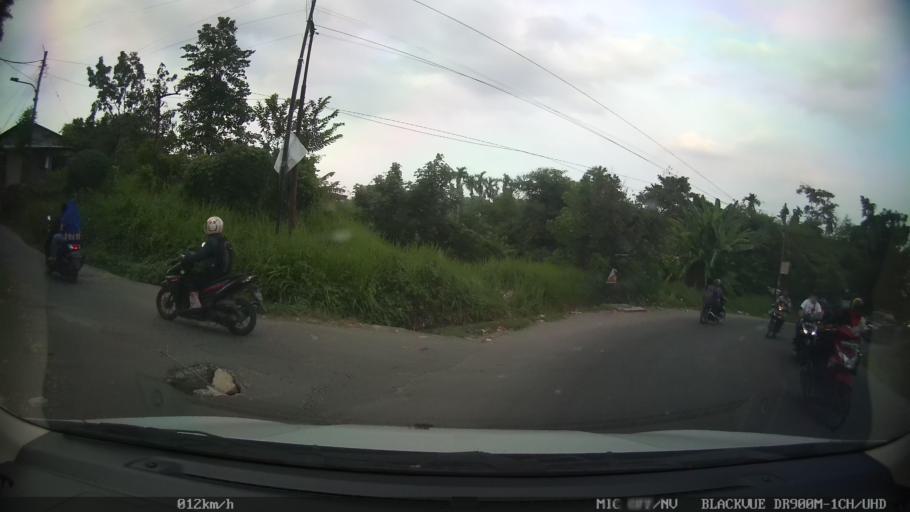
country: ID
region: North Sumatra
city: Sunggal
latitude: 3.5648
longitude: 98.6071
